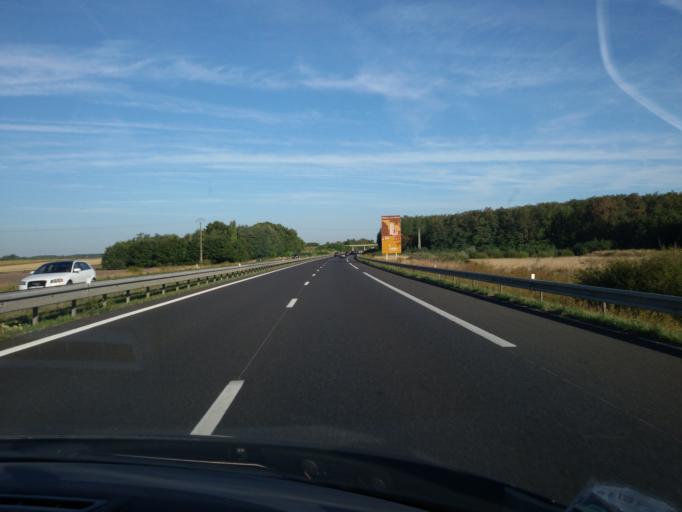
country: FR
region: Centre
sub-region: Departement du Cher
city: Mehun-sur-Yevre
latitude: 47.1078
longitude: 2.2086
